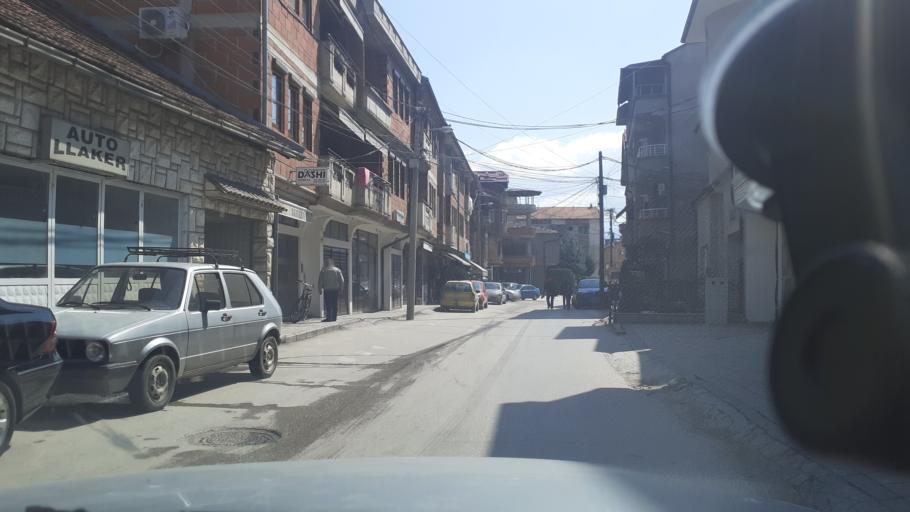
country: MK
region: Tetovo
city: Tetovo
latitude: 42.0038
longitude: 20.9681
